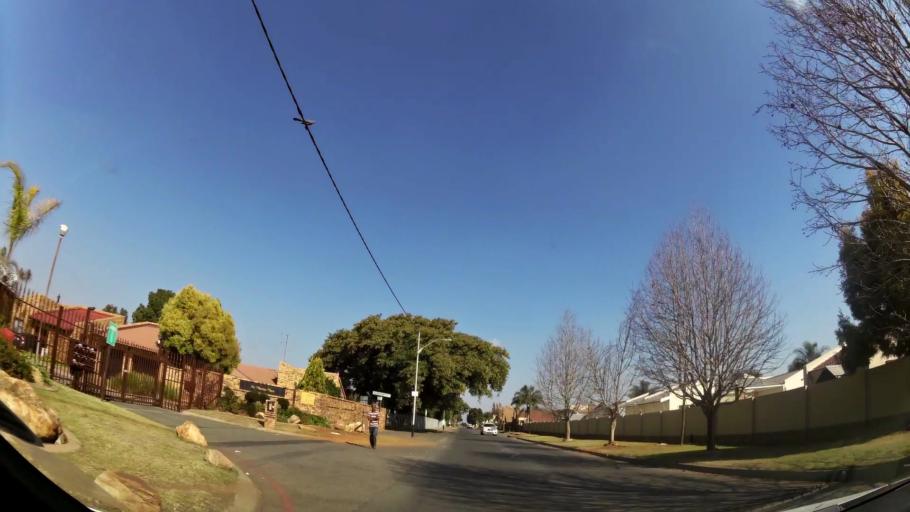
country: ZA
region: Gauteng
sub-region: Ekurhuleni Metropolitan Municipality
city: Boksburg
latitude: -26.1829
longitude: 28.2766
